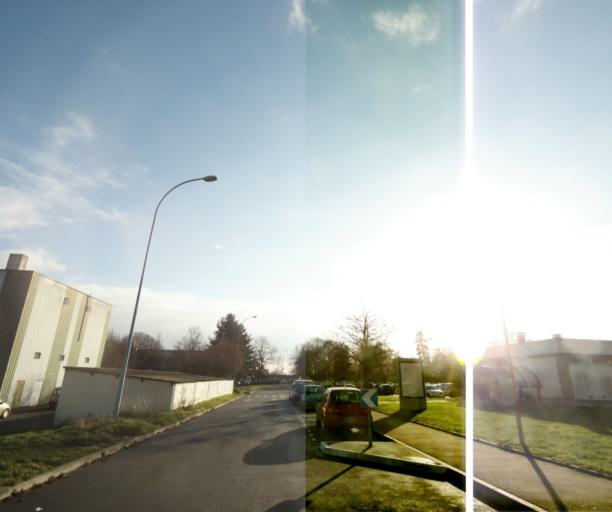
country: FR
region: Pays de la Loire
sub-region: Departement de la Sarthe
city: La Chapelle-Saint-Aubin
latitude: 48.0173
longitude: 0.1581
